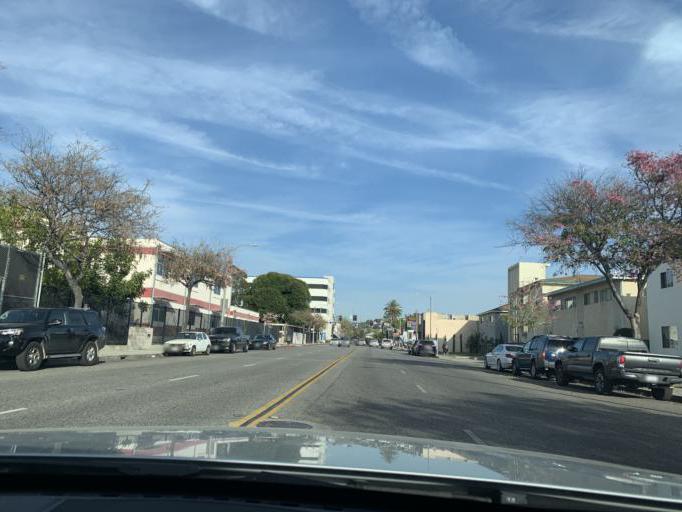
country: US
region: California
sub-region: Los Angeles County
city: Glendale
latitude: 34.1335
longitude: -118.2536
